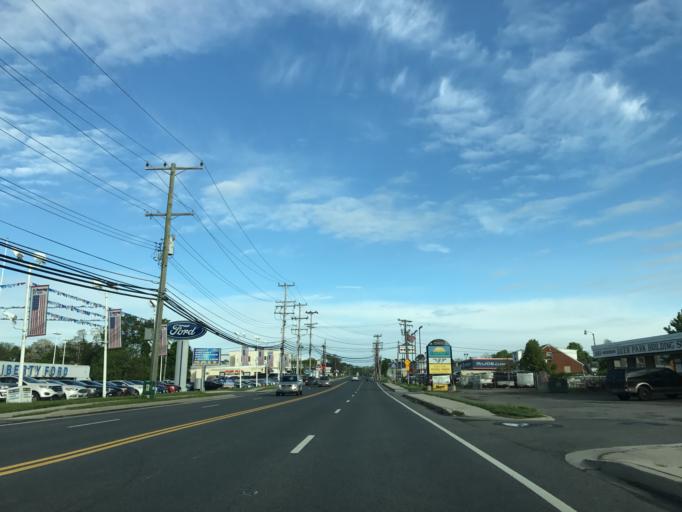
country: US
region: Maryland
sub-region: Baltimore County
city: Randallstown
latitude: 39.3722
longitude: -76.8060
